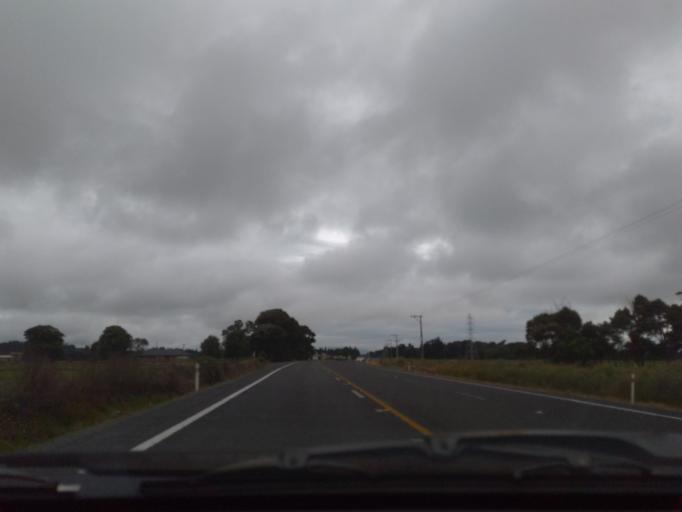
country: NZ
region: Northland
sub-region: Whangarei
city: Ruakaka
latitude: -35.9943
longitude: 174.4205
